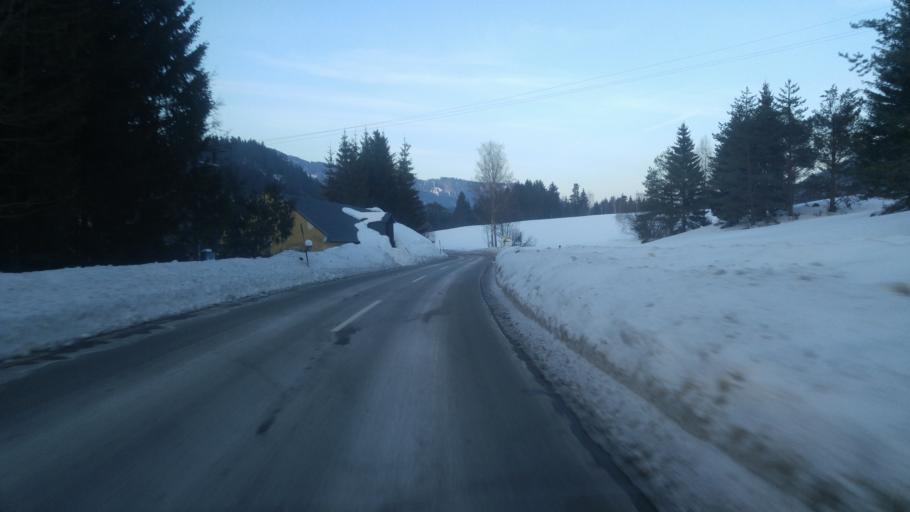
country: AT
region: Lower Austria
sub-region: Politischer Bezirk Wiener Neustadt
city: Rohr im Gebirge
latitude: 47.8731
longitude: 15.7044
